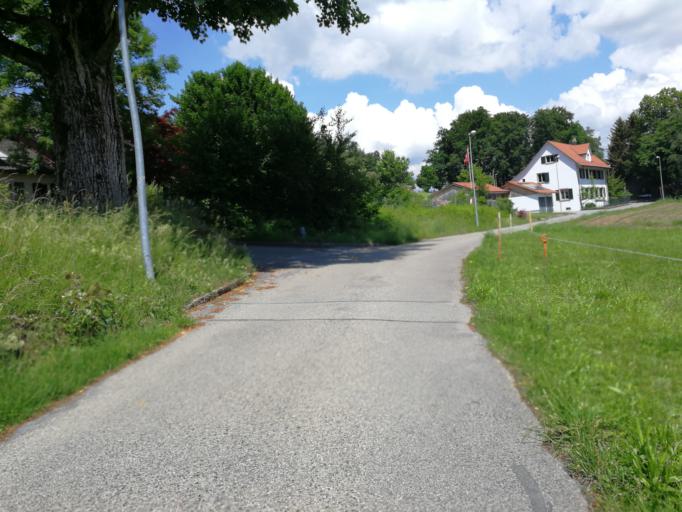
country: CH
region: Zurich
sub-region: Bezirk Meilen
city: Uetikon / Grossdorf
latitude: 47.2783
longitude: 8.6859
